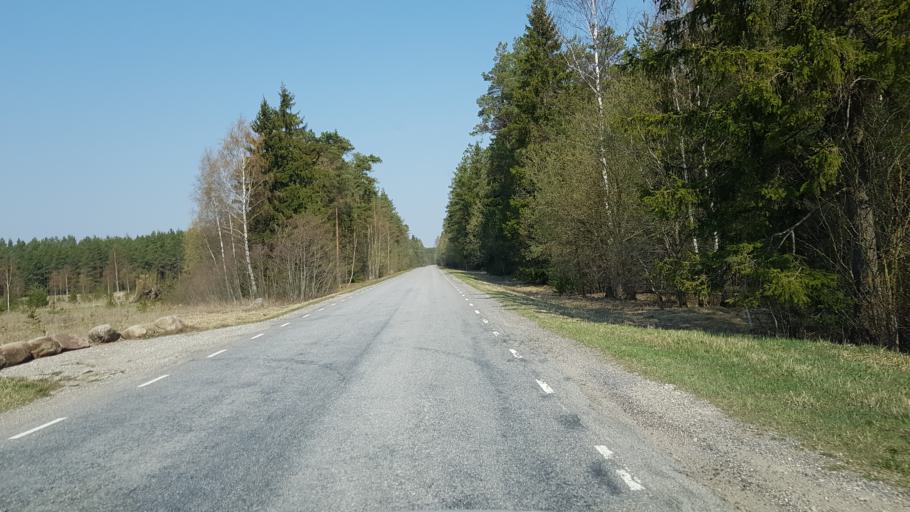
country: EE
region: Raplamaa
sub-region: Kohila vald
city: Kohila
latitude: 59.1875
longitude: 24.6614
